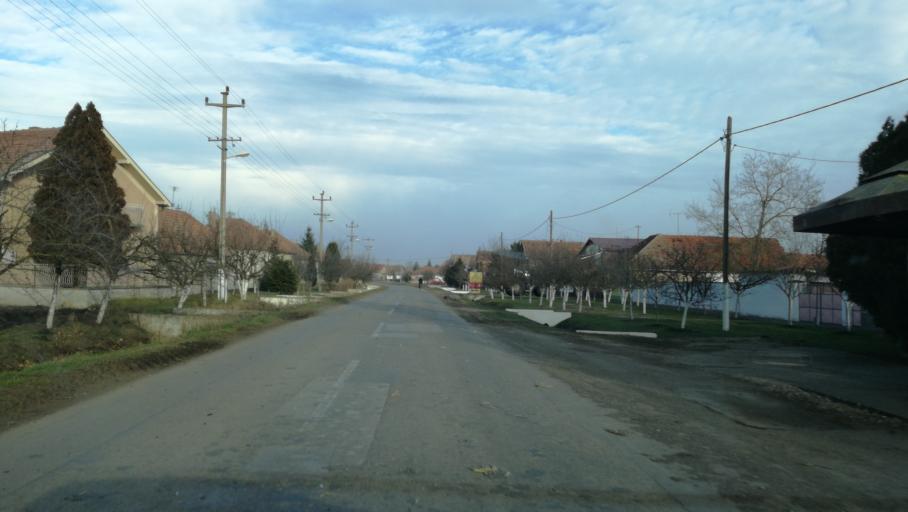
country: RS
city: Novi Kozarci
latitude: 45.7745
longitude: 20.5996
